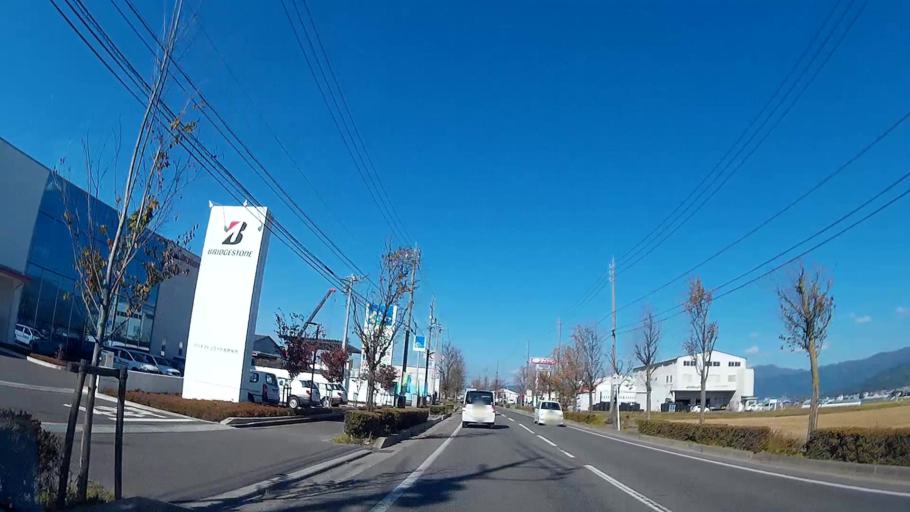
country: JP
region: Nagano
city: Matsumoto
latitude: 36.1774
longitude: 137.9491
